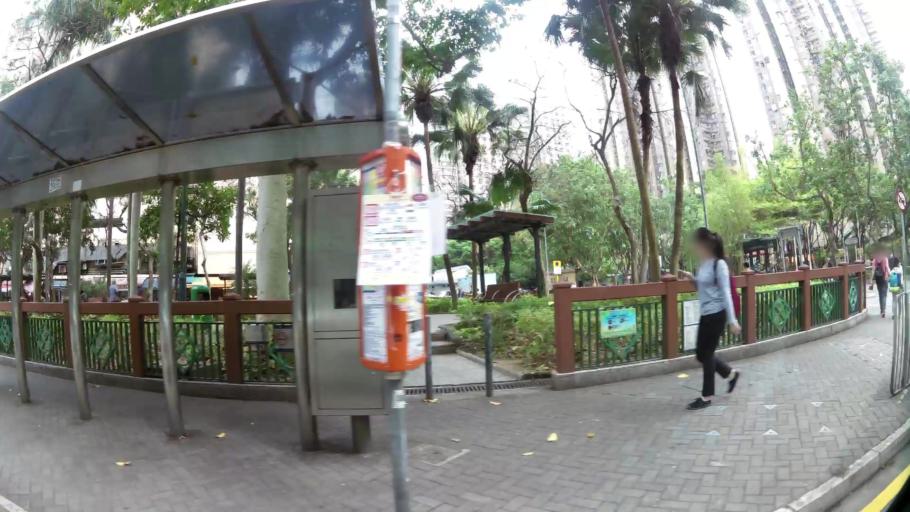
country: HK
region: Wanchai
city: Wan Chai
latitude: 22.2636
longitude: 114.2390
